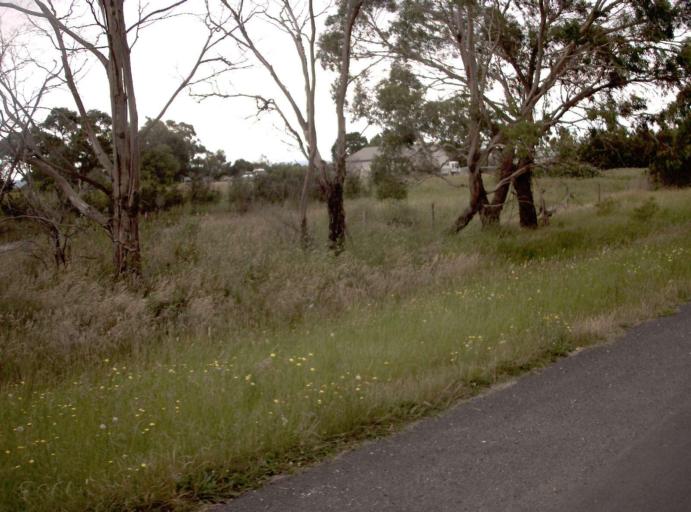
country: AU
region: Victoria
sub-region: Casey
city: Tooradin
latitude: -38.2139
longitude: 145.4128
